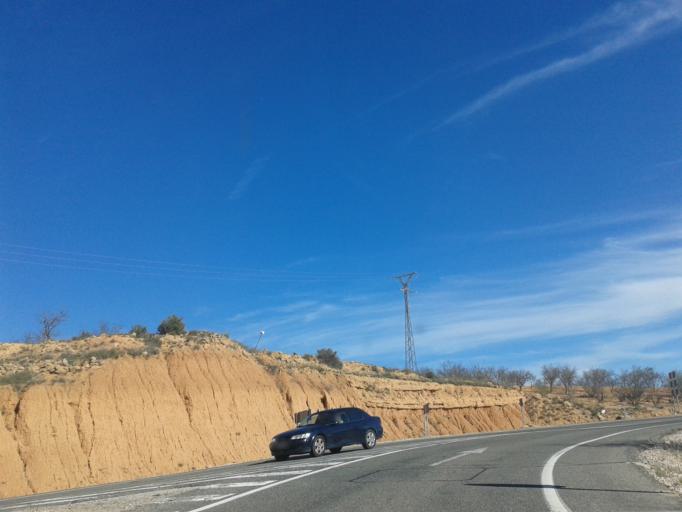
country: ES
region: Castille-La Mancha
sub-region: Provincia de Albacete
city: Caudete
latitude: 38.7332
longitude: -0.9402
